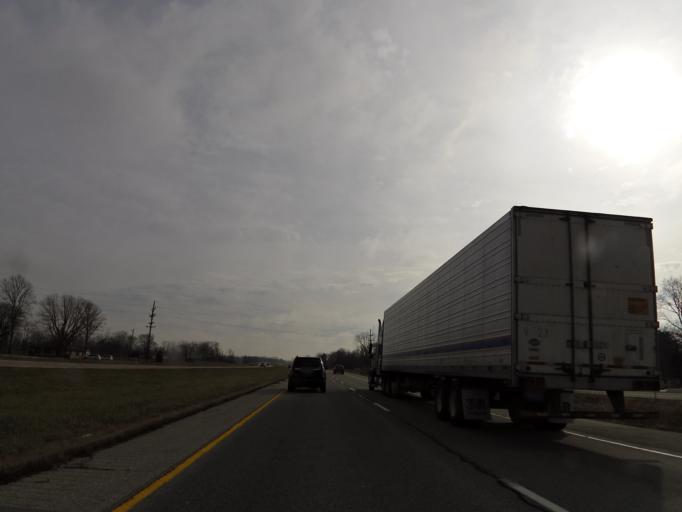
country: US
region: Indiana
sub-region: Hancock County
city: New Palestine
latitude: 39.6351
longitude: -85.8976
